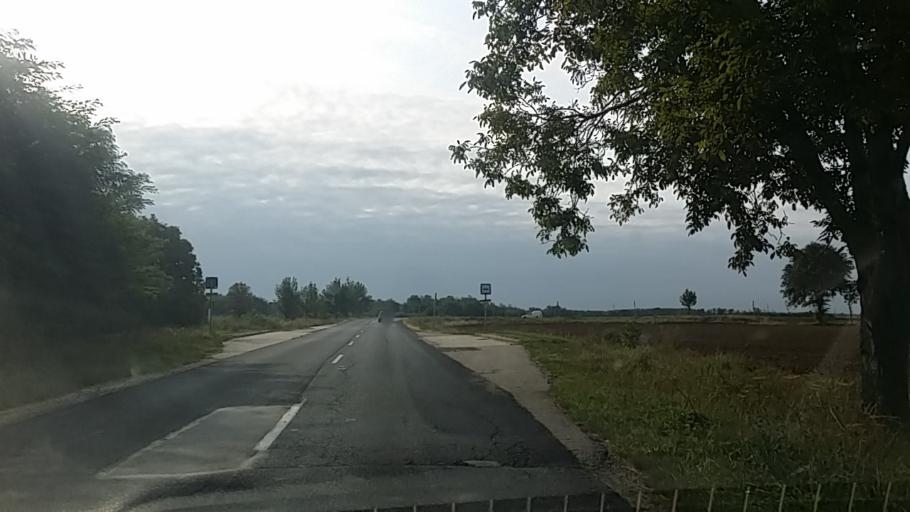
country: HU
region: Gyor-Moson-Sopron
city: Fertoszentmiklos
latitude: 47.5986
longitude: 16.9152
